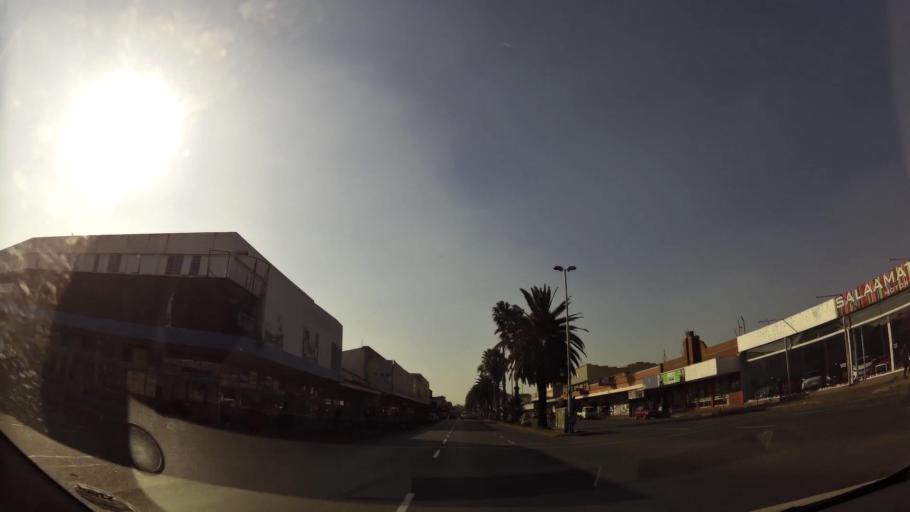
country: ZA
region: Gauteng
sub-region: West Rand District Municipality
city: Randfontein
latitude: -26.1794
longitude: 27.7042
